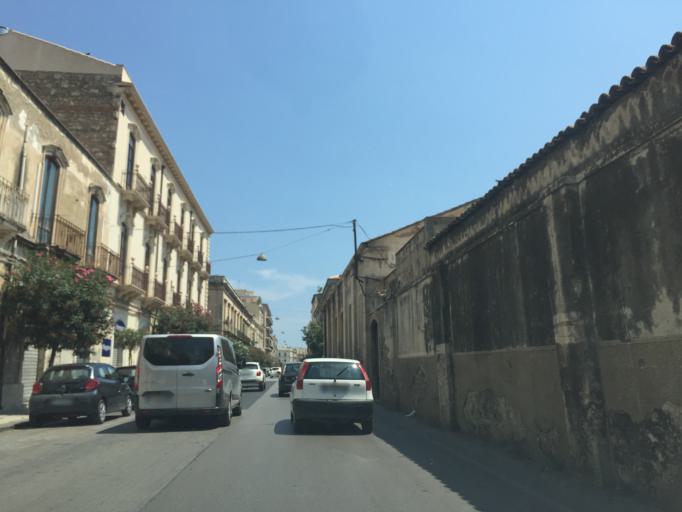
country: IT
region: Sicily
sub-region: Provincia di Siracusa
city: Siracusa
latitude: 37.0655
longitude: 15.2862
